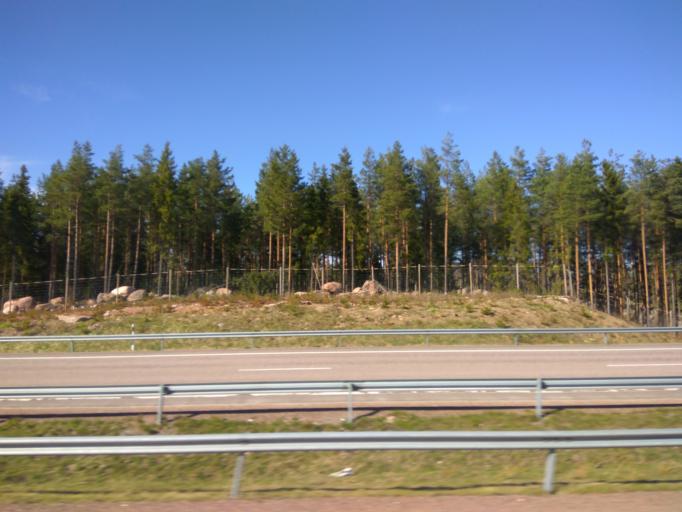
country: FI
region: Uusimaa
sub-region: Loviisa
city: Lovisa
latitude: 60.4899
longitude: 26.3342
